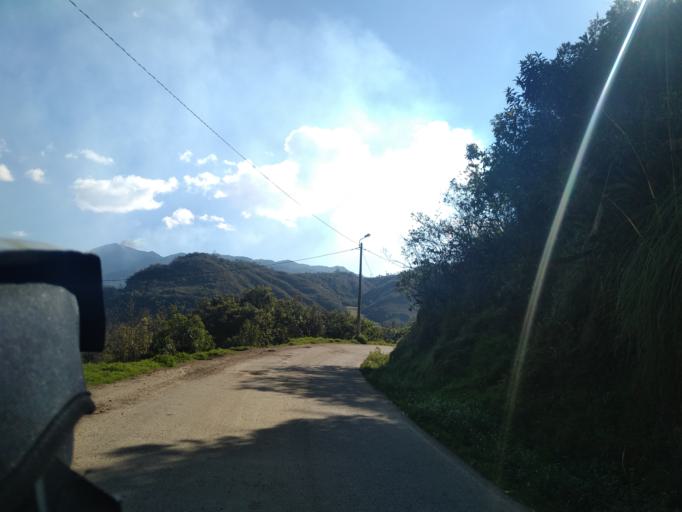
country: PE
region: Amazonas
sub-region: Provincia de Chachapoyas
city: Montevideo
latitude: -6.7263
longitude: -77.8280
